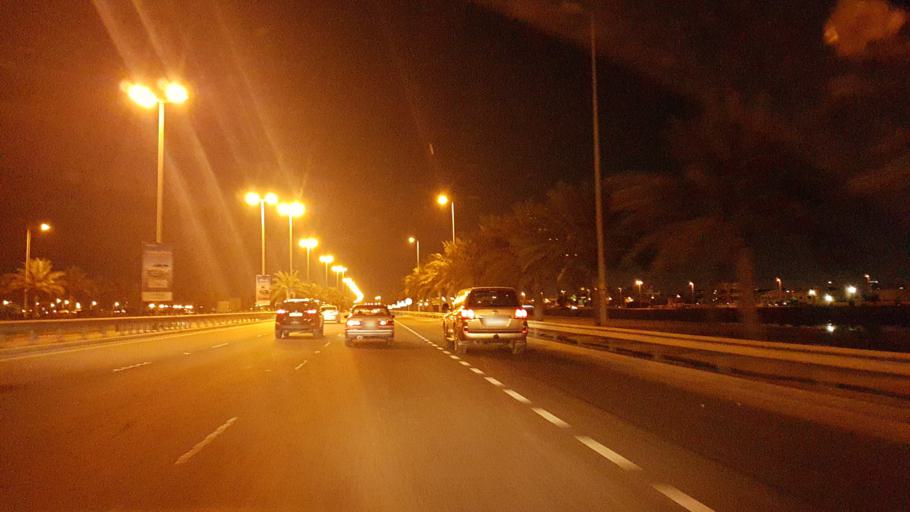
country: BH
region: Muharraq
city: Al Hadd
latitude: 26.2530
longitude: 50.6595
